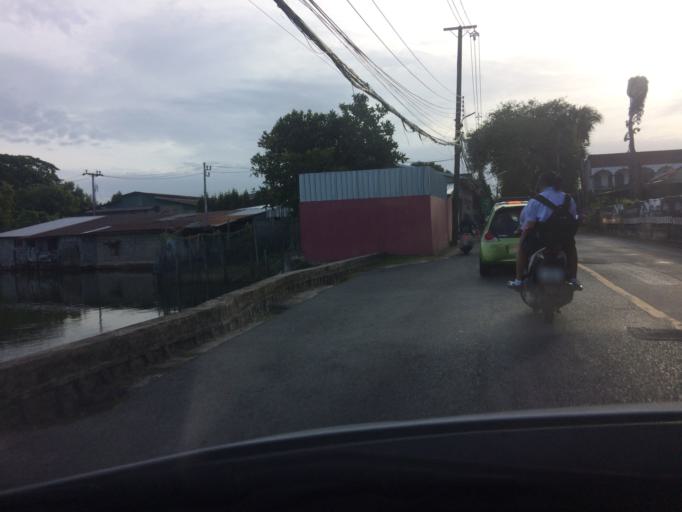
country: TH
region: Phuket
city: Ban Talat Yai
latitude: 7.8733
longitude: 98.3971
